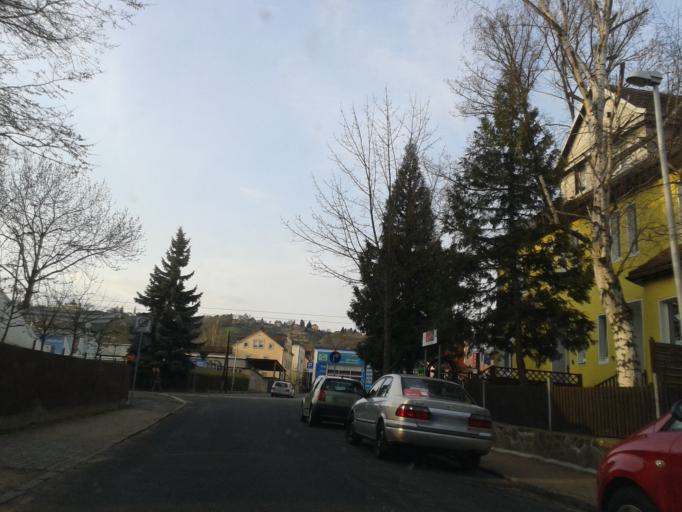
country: DE
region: Saxony
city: Radebeul
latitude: 51.1034
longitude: 13.6714
